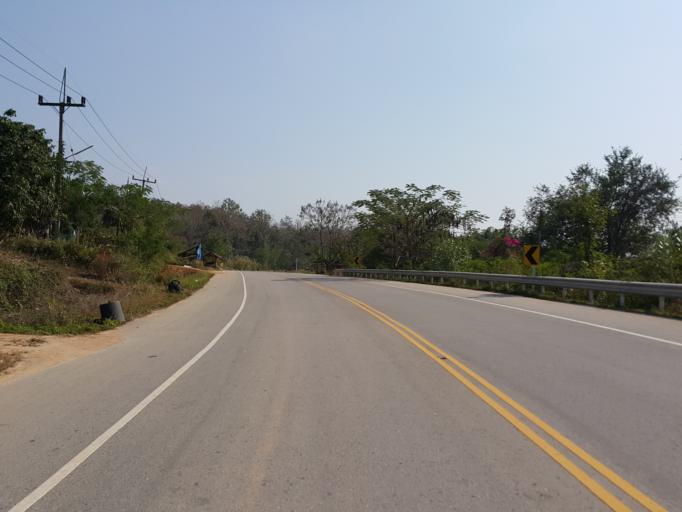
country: TH
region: Lampang
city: Mueang Pan
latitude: 18.8528
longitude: 99.5997
